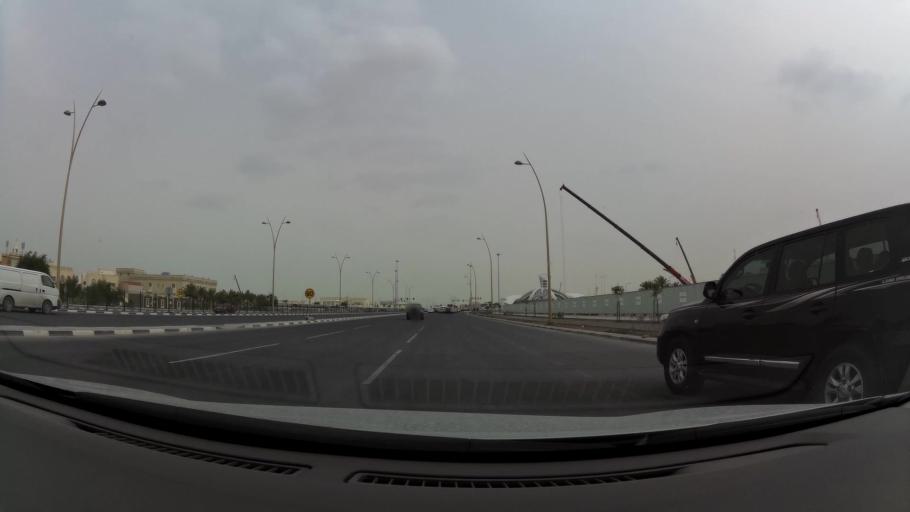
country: QA
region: Baladiyat ad Dawhah
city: Doha
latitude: 25.2413
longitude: 51.5456
